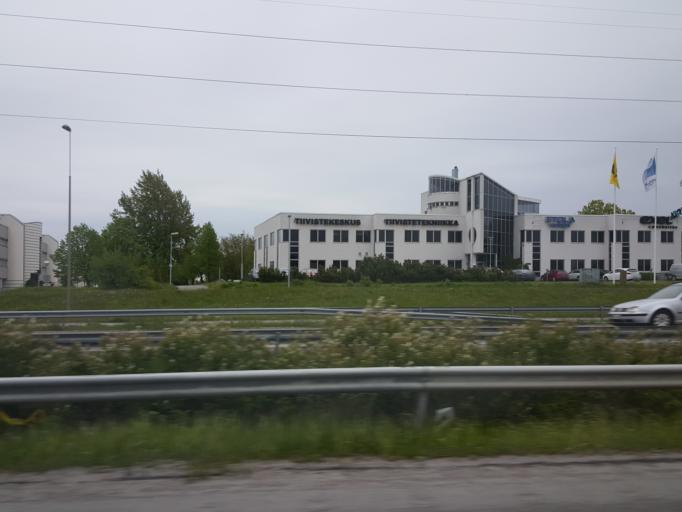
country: FI
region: Uusimaa
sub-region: Helsinki
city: Vantaa
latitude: 60.2921
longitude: 24.9822
